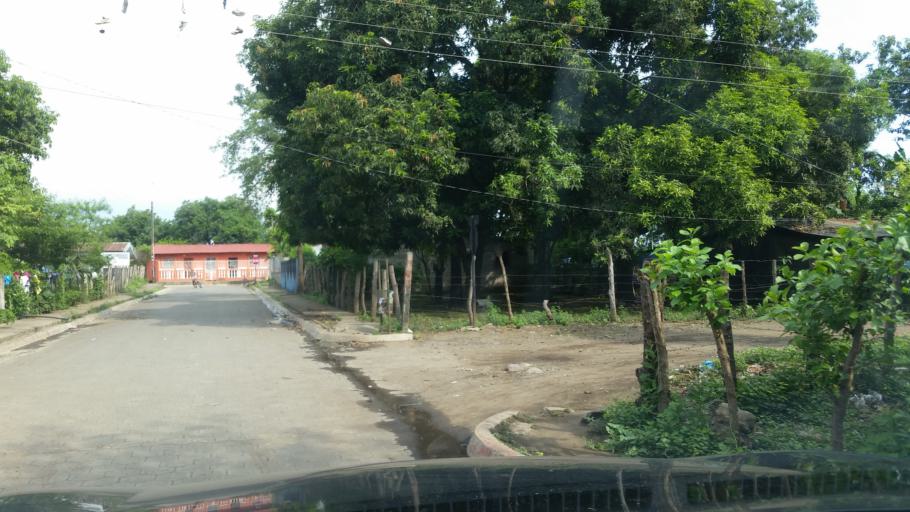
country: NI
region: Chinandega
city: Puerto Morazan
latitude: 12.7648
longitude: -87.1316
